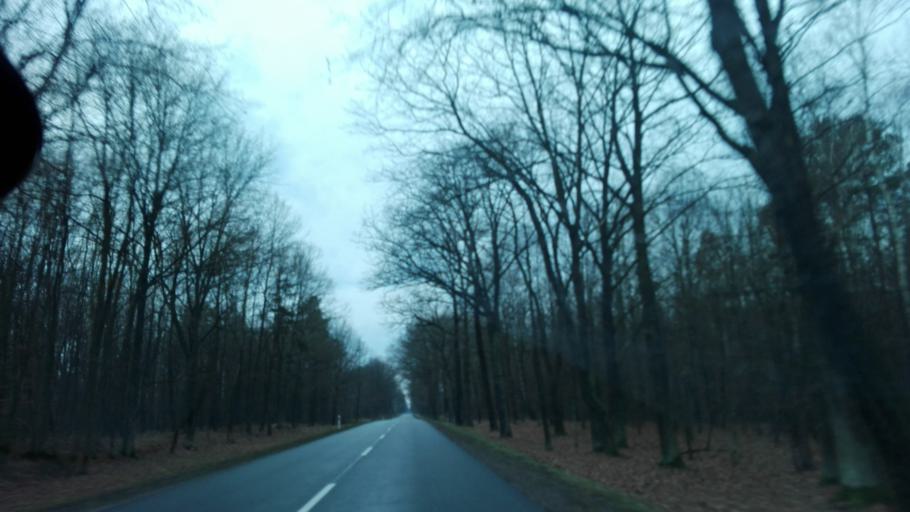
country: PL
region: Lublin Voivodeship
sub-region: Powiat radzynski
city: Wohyn
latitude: 51.7821
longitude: 22.7323
